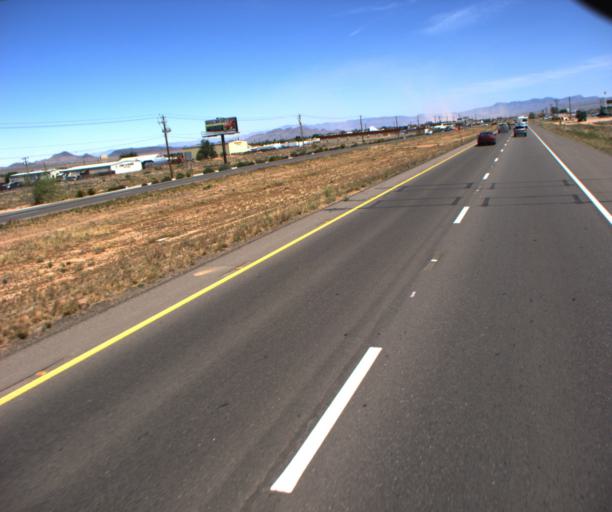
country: US
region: Arizona
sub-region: Mohave County
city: New Kingman-Butler
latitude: 35.2319
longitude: -113.9963
